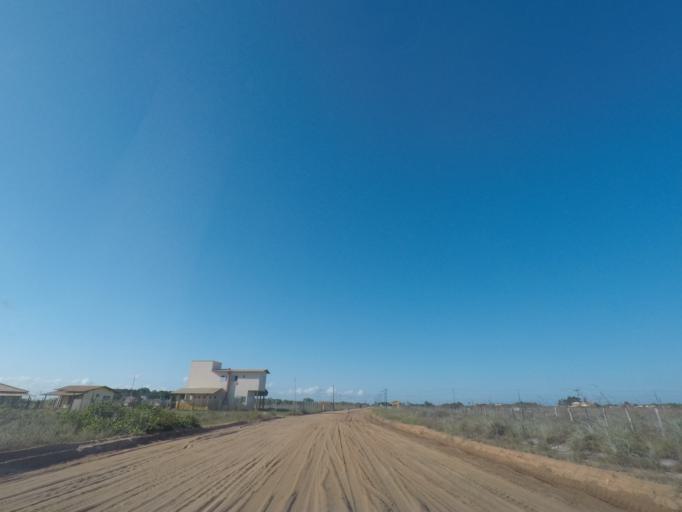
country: BR
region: Bahia
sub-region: Camamu
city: Camamu
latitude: -13.9375
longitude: -38.9466
